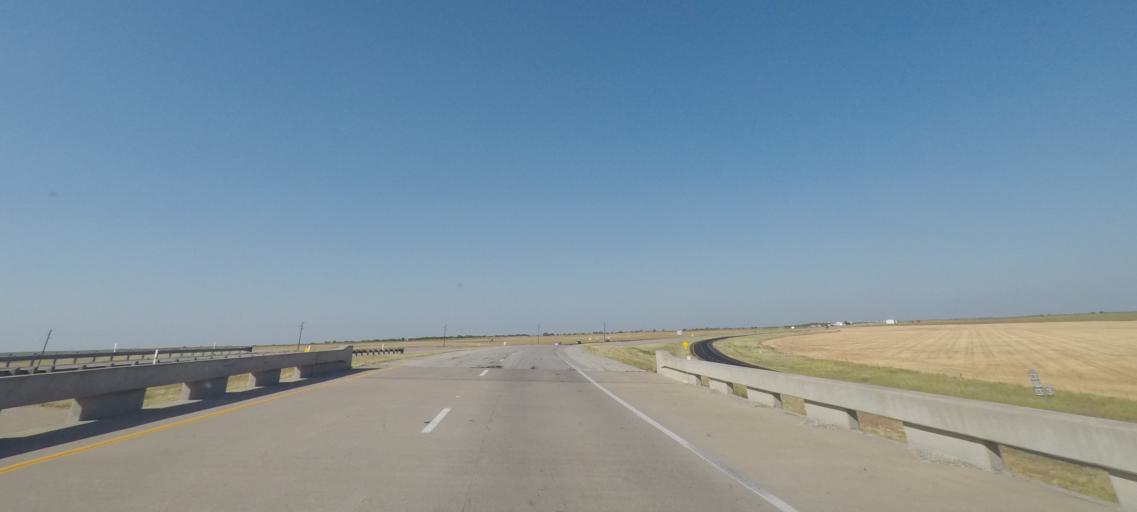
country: US
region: Texas
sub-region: Baylor County
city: Seymour
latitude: 33.6154
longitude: -99.2426
